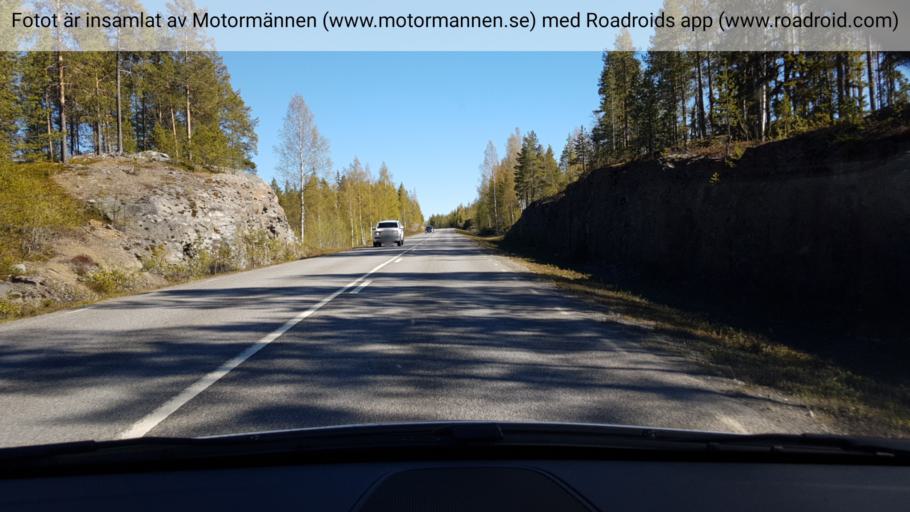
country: SE
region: Jaemtland
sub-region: Stroemsunds Kommun
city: Stroemsund
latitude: 64.3205
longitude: 15.2037
